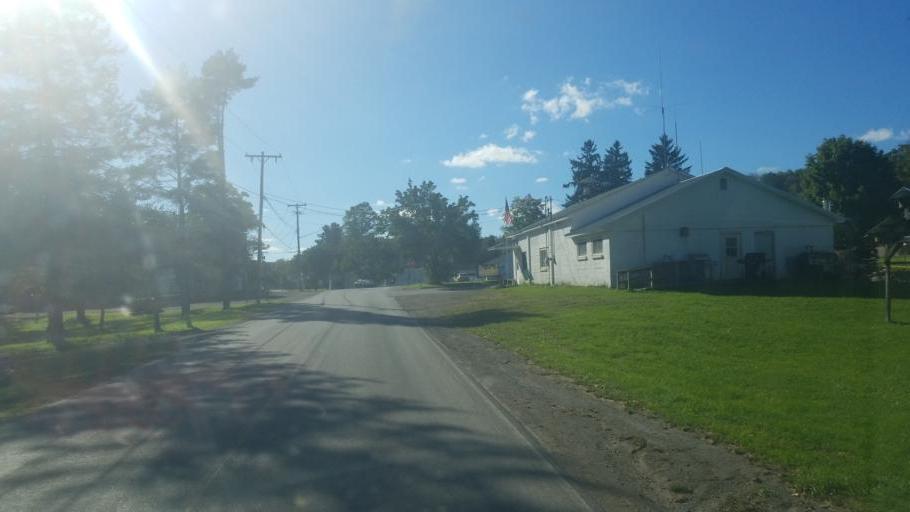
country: US
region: New York
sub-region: Allegany County
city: Cuba
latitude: 42.2755
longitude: -78.2253
